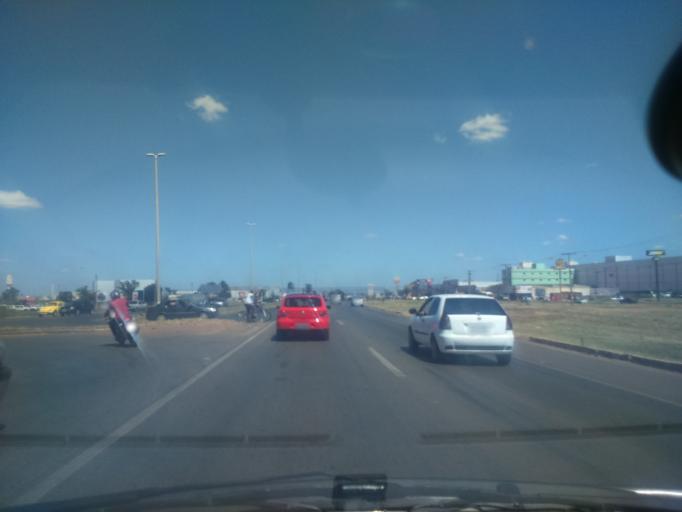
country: BR
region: Goias
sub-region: Luziania
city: Luziania
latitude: -16.0740
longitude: -47.9854
